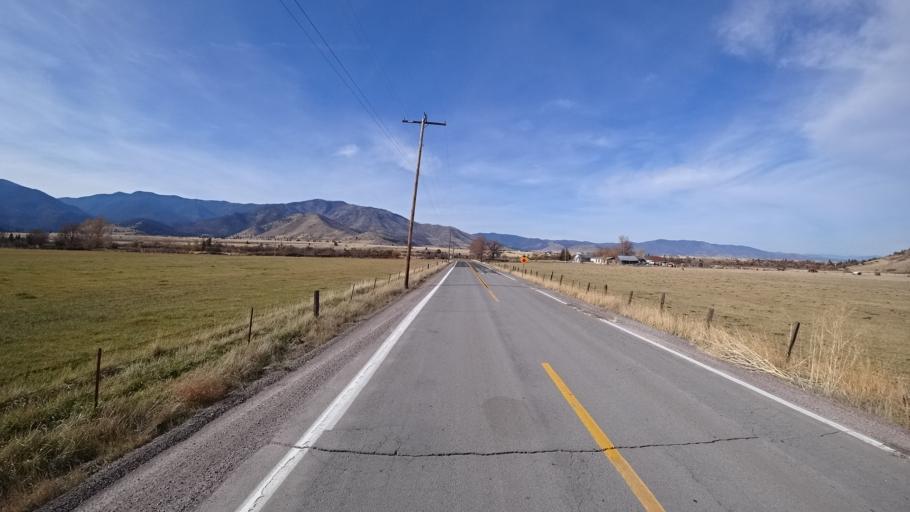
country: US
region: California
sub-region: Siskiyou County
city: Weed
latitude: 41.4677
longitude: -122.4321
